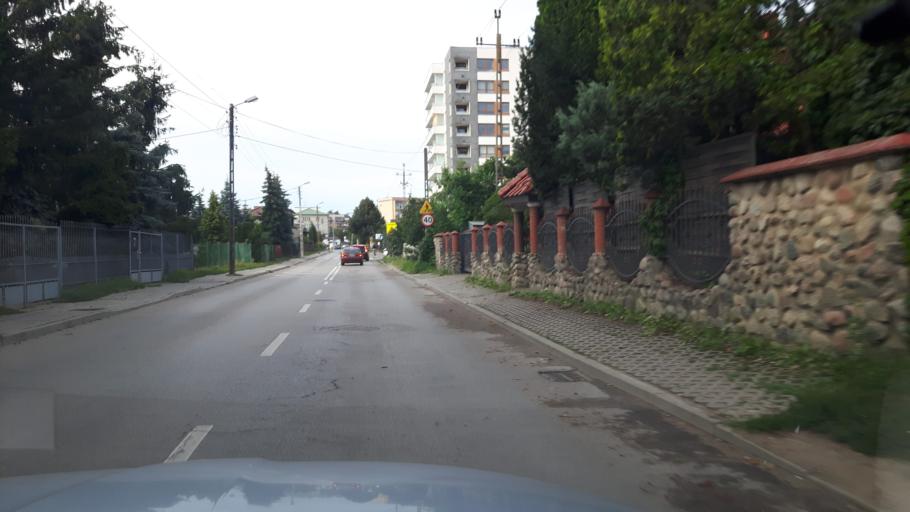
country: PL
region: Masovian Voivodeship
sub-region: Powiat wolominski
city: Marki
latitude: 52.3271
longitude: 21.1006
